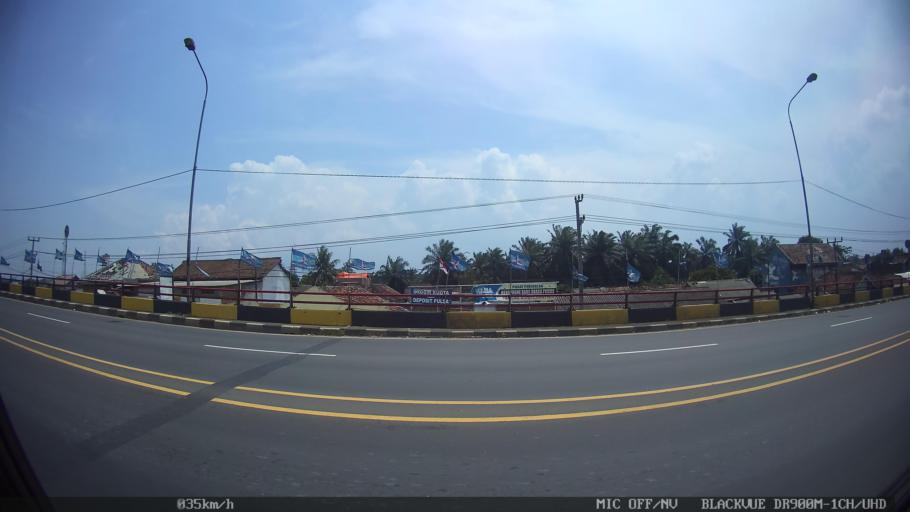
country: ID
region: Lampung
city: Natar
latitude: -5.3194
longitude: 105.1976
